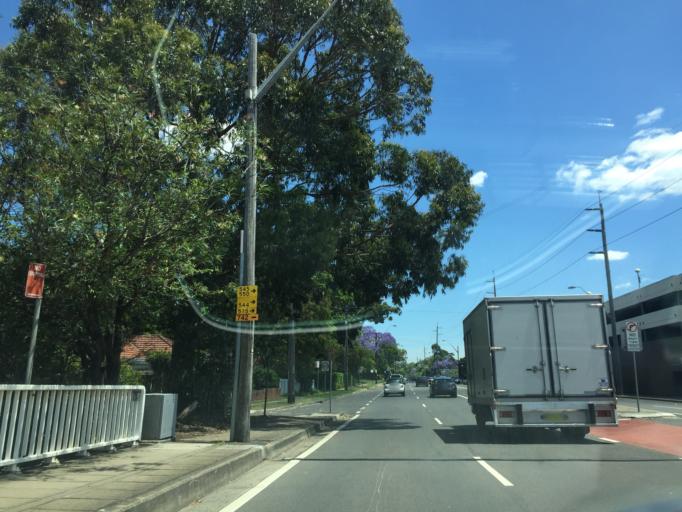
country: AU
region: New South Wales
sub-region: Ryde
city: Denistone
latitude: -33.7925
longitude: 151.0824
